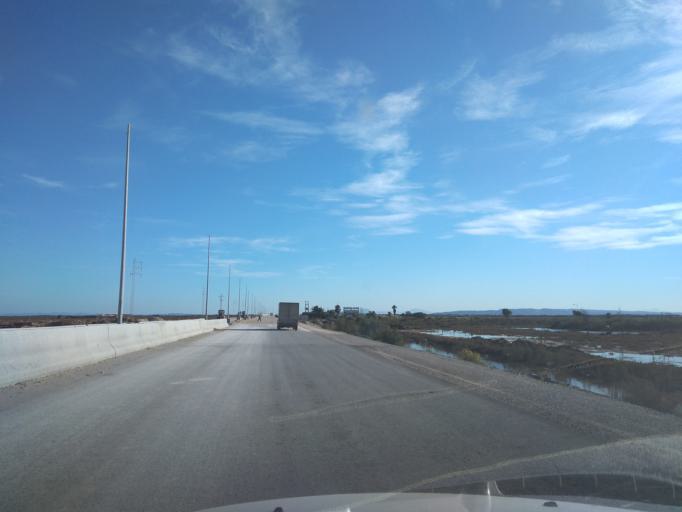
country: TN
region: Ariana
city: Qal'at al Andalus
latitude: 37.0448
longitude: 10.1271
